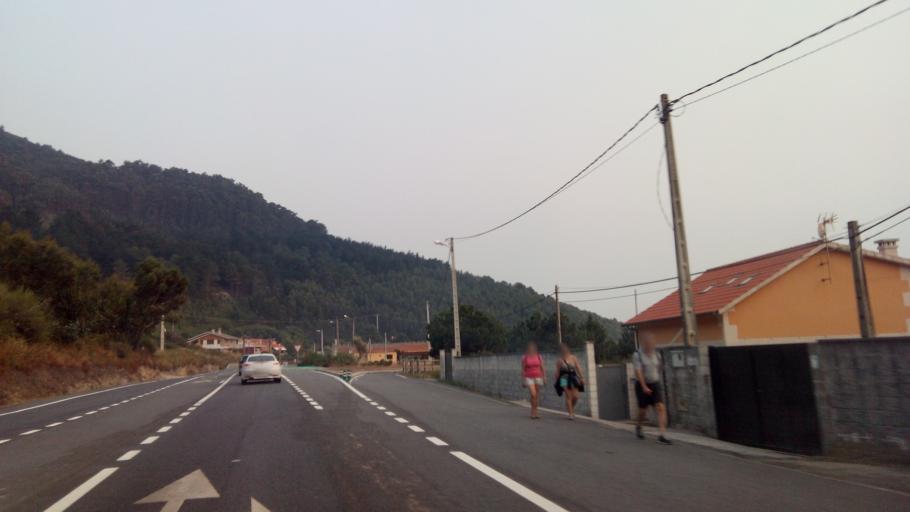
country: ES
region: Galicia
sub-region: Provincia de Pontevedra
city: Baiona
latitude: 42.0846
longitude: -8.8906
